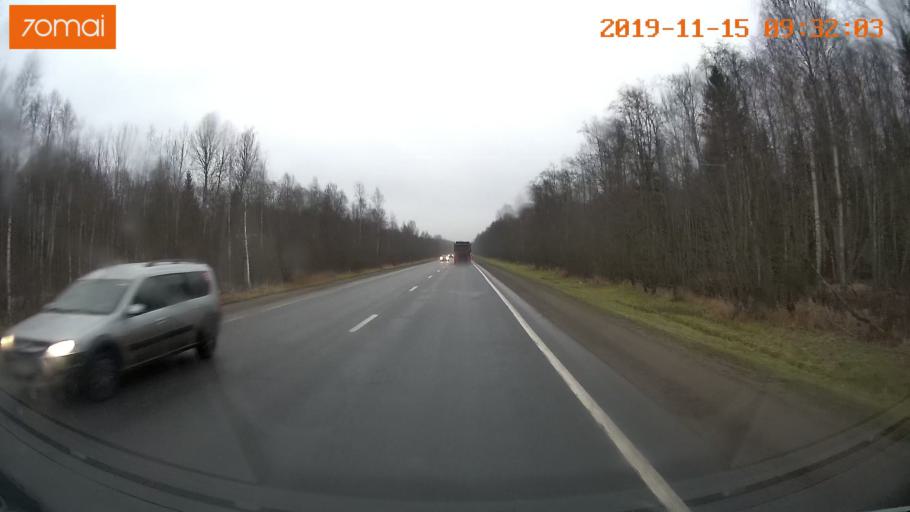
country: RU
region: Vologda
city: Sheksna
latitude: 59.2731
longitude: 38.3253
